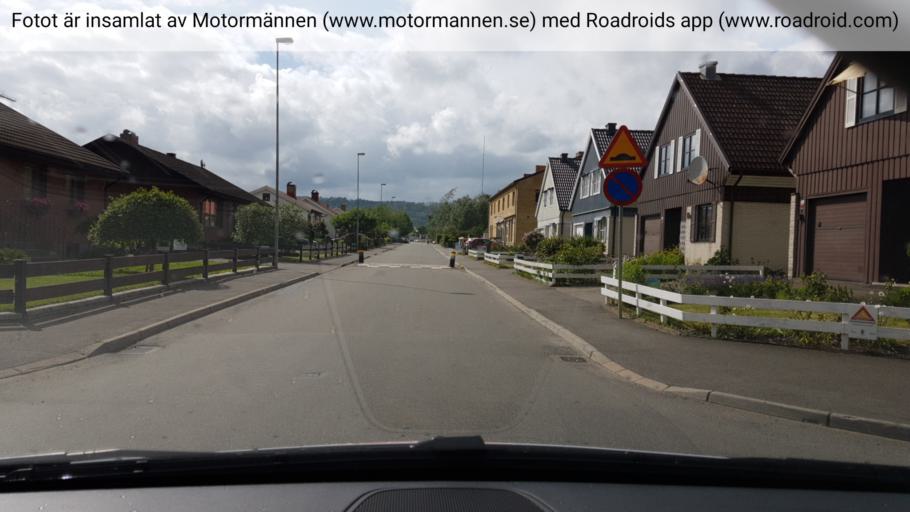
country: SE
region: Vaestra Goetaland
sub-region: Skovde Kommun
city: Skoevde
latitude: 58.4008
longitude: 13.8590
